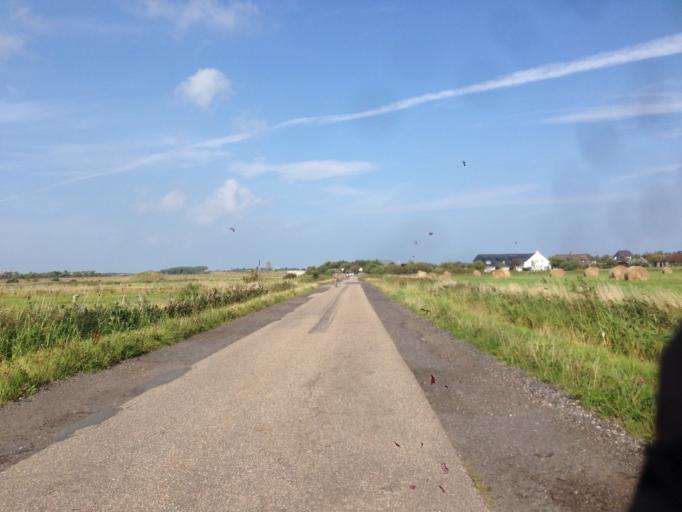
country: DE
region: Schleswig-Holstein
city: Keitum
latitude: 54.8887
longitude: 8.3530
